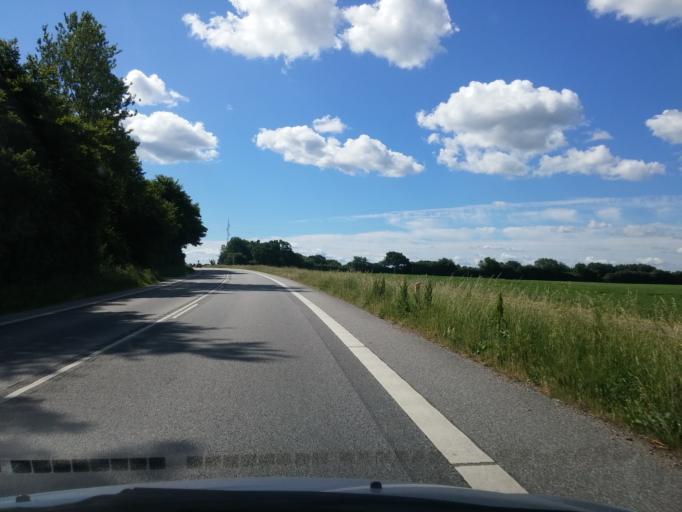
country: DK
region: South Denmark
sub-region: Haderslev Kommune
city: Haderslev
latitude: 55.2735
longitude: 9.4658
